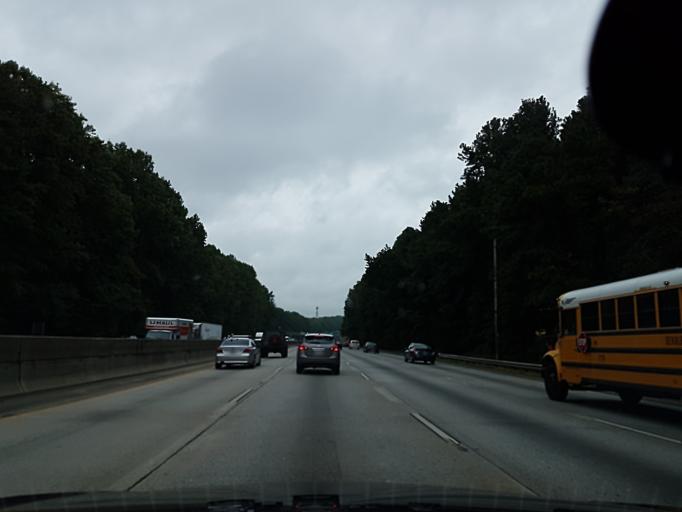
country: US
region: Georgia
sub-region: DeKalb County
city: Tucker
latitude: 33.8634
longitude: -84.2484
